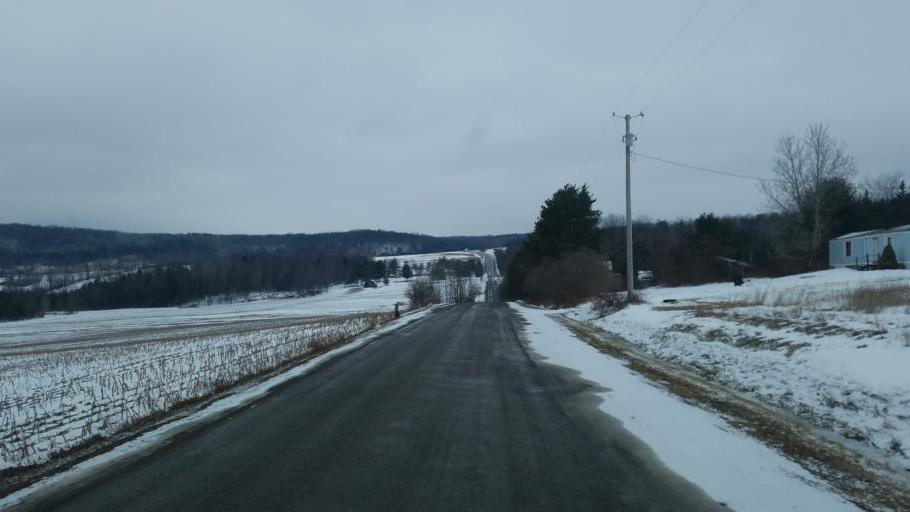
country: US
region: Pennsylvania
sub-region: Tioga County
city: Elkland
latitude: 42.1119
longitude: -77.3978
